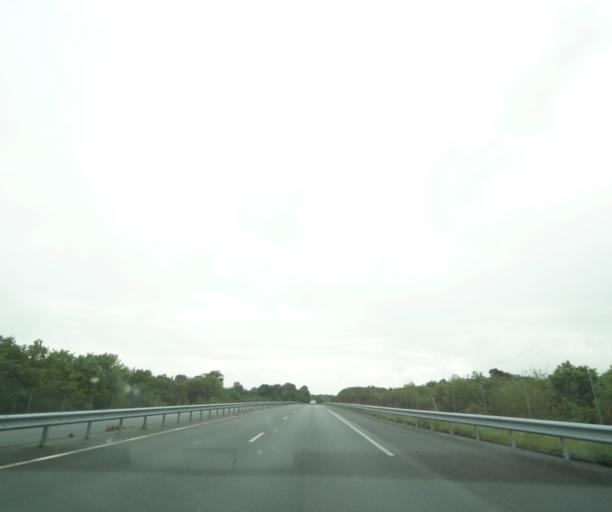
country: FR
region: Poitou-Charentes
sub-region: Departement de la Charente-Maritime
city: Chermignac
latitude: 45.7090
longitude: -0.7099
